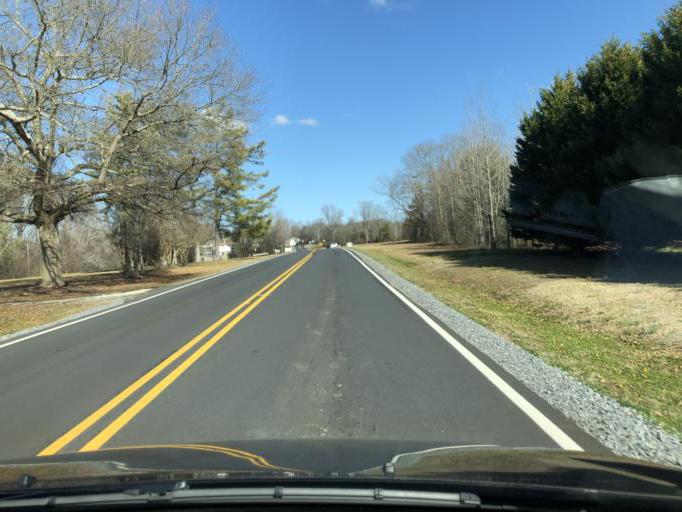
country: US
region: North Carolina
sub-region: Cleveland County
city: Shelby
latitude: 35.2215
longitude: -81.5327
